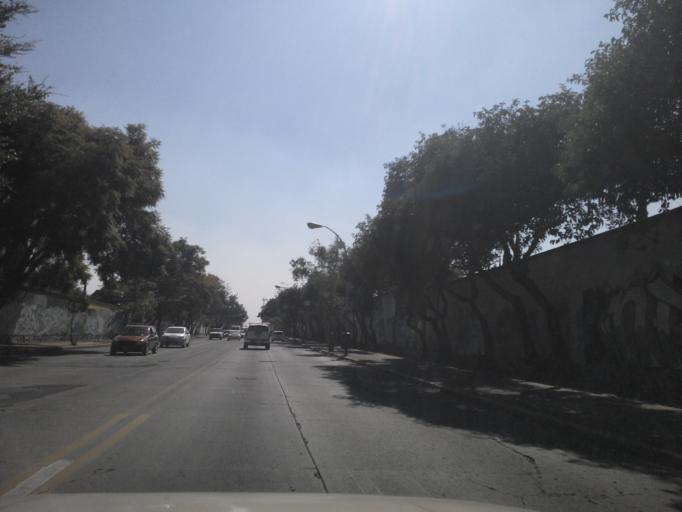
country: MX
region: Jalisco
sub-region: Zapopan
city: Zapopan
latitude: 20.6929
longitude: -103.3586
